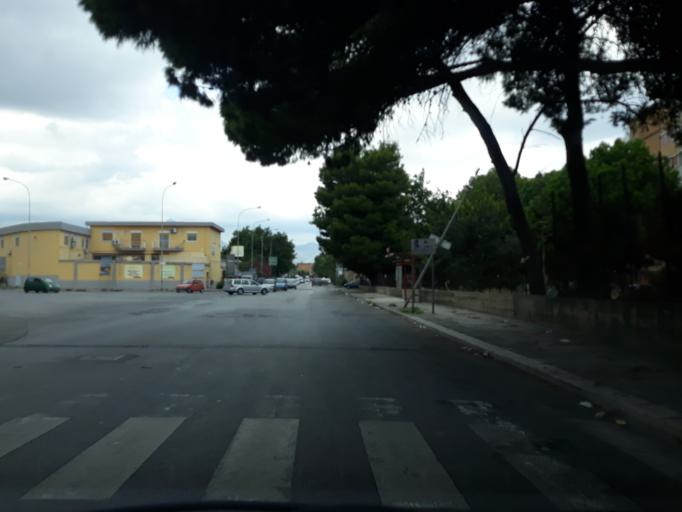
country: IT
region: Sicily
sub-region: Palermo
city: Ciaculli
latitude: 38.0953
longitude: 13.3985
